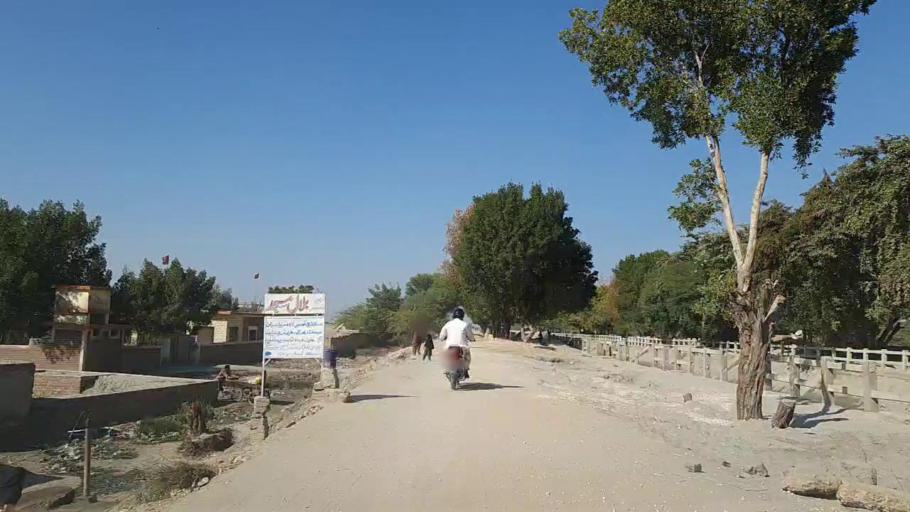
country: PK
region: Sindh
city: Nawabshah
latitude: 26.2584
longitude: 68.4173
